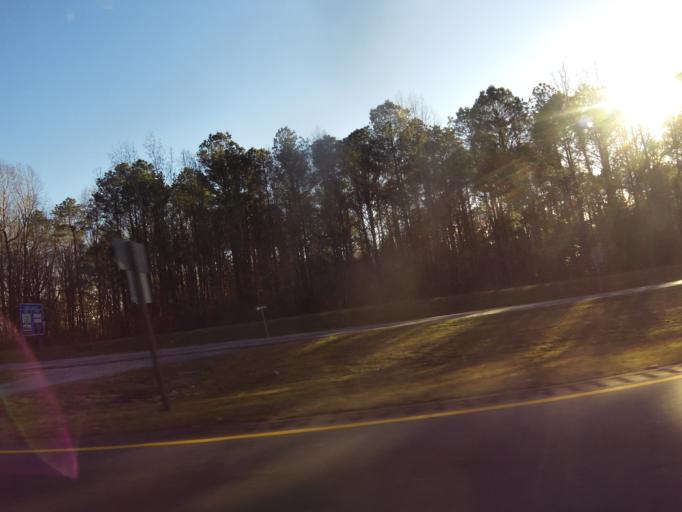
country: US
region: Virginia
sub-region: City of Suffolk
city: Suffolk
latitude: 36.7689
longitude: -76.5926
